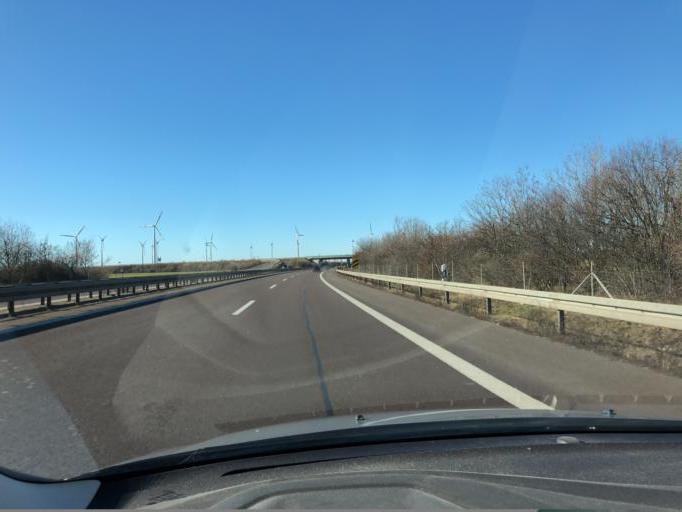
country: DE
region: Saxony-Anhalt
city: Frose
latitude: 51.7728
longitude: 11.4138
